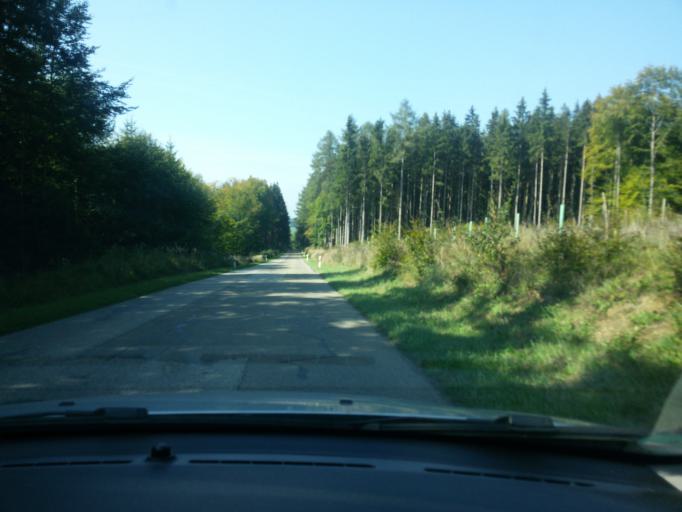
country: DE
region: Bavaria
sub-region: Swabia
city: Scherstetten
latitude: 48.1838
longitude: 10.6617
